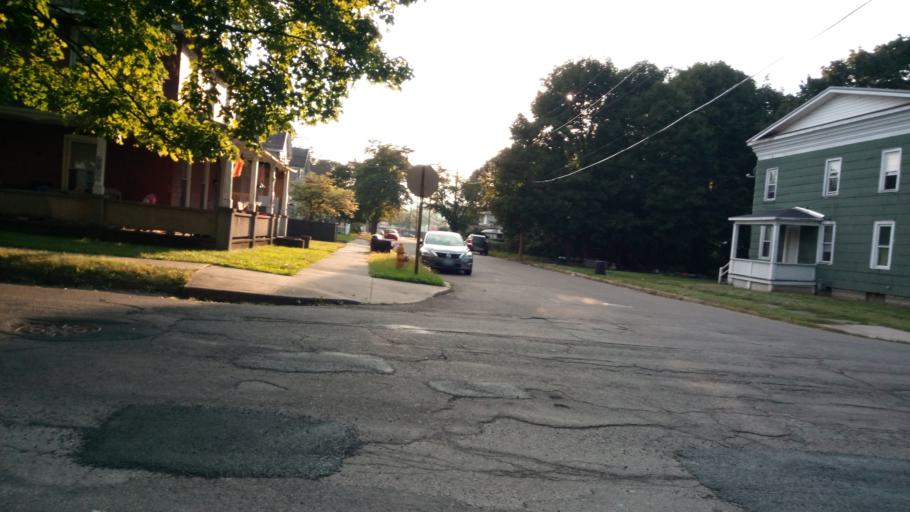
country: US
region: New York
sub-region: Chemung County
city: Elmira
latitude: 42.1017
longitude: -76.8010
